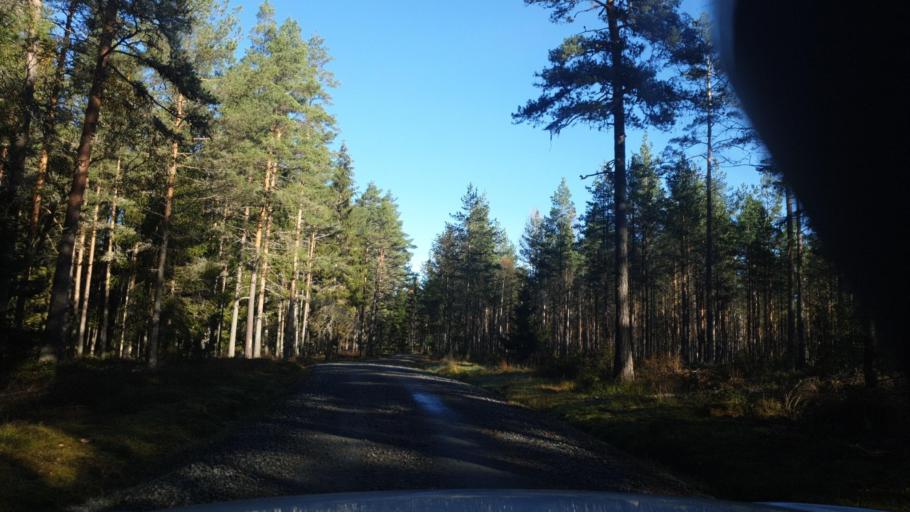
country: SE
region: Vaermland
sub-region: Karlstads Kommun
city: Valberg
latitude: 59.4555
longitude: 13.0967
